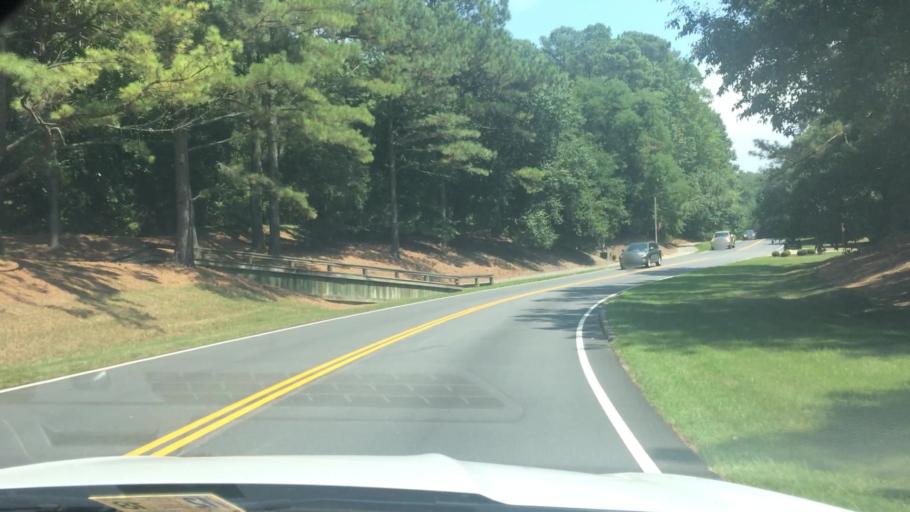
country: US
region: Virginia
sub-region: City of Williamsburg
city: Williamsburg
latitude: 37.2312
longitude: -76.6514
